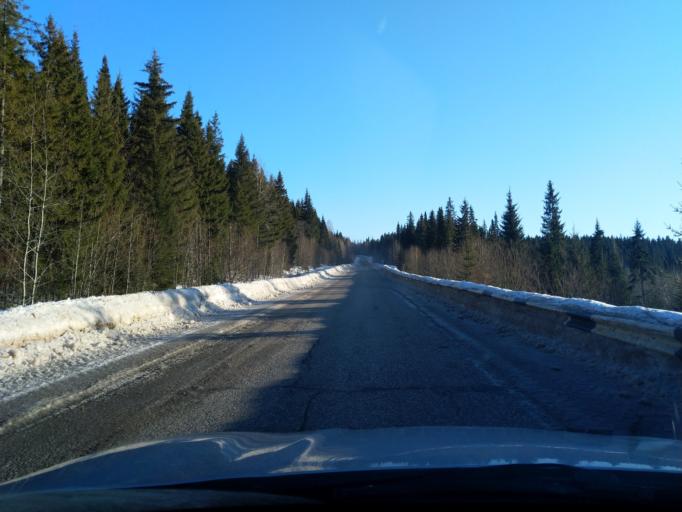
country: RU
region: Perm
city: Polazna
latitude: 58.3037
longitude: 56.4730
